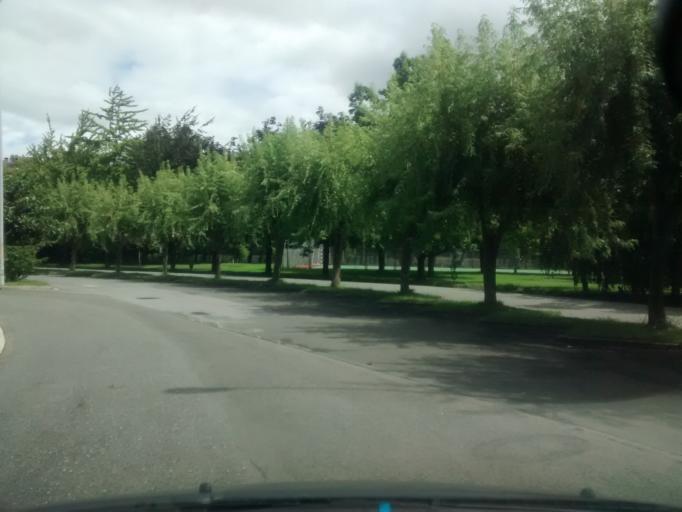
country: ES
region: Basque Country
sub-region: Provincia de Guipuzcoa
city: San Sebastian
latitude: 43.3089
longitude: -1.9758
